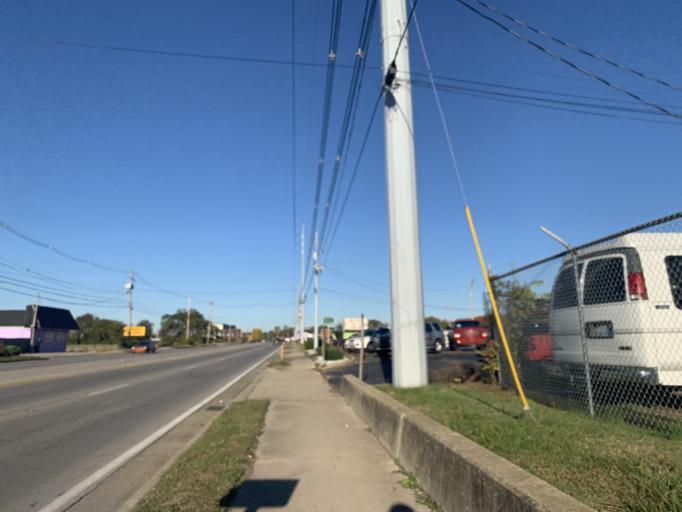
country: US
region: Kentucky
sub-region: Jefferson County
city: Shively
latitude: 38.1986
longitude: -85.7973
